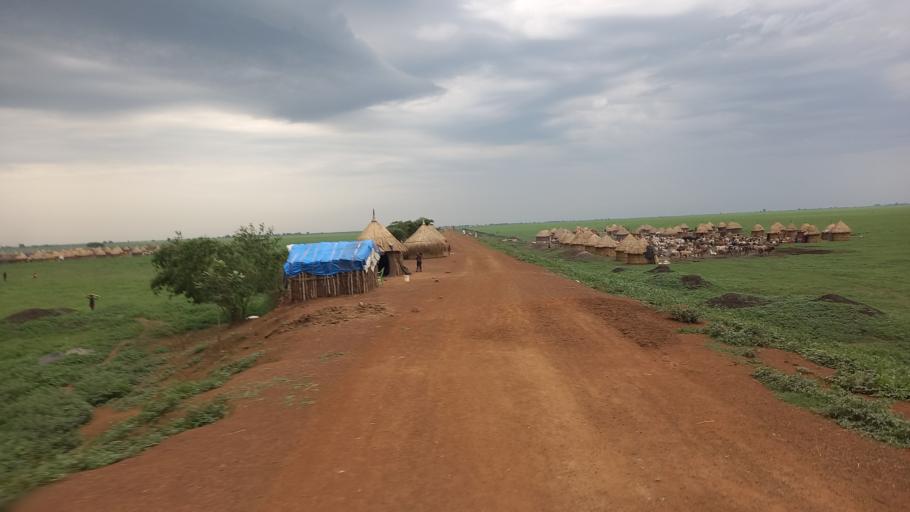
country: ET
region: Gambela
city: Gambela
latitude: 8.3628
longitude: 33.8228
